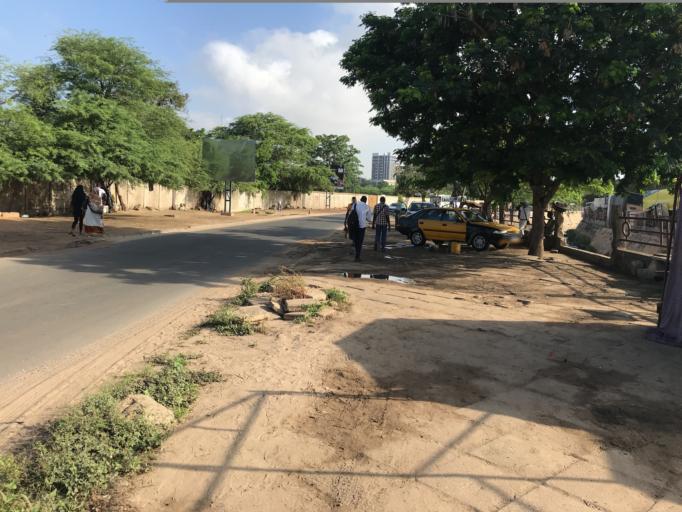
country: SN
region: Dakar
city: Dakar
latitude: 14.6859
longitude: -17.4608
